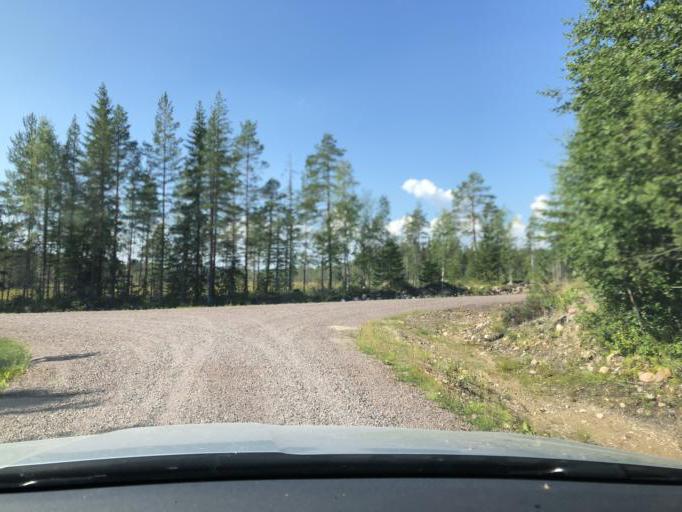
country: SE
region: Dalarna
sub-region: Orsa Kommun
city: Orsa
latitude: 61.2662
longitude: 14.7379
